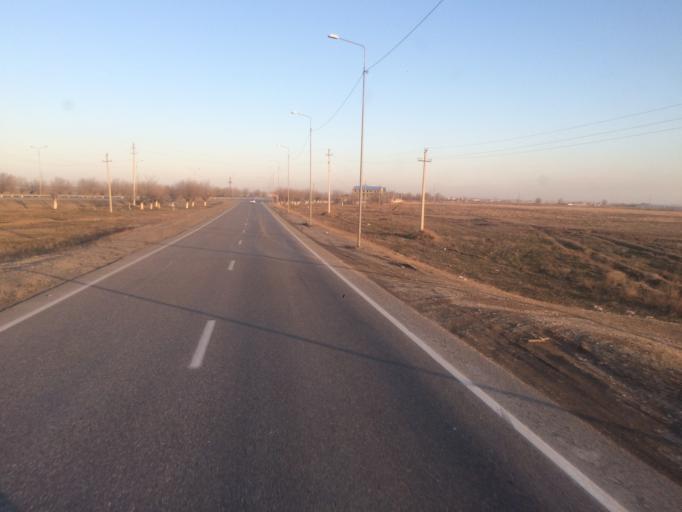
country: KZ
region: Ongtustik Qazaqstan
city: Turkestan
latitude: 43.2735
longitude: 68.3382
